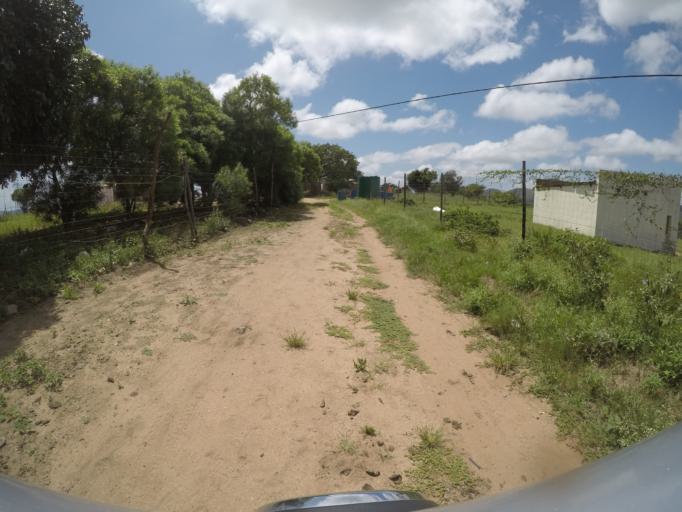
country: ZA
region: KwaZulu-Natal
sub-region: uThungulu District Municipality
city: Empangeni
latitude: -28.5782
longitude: 31.8422
